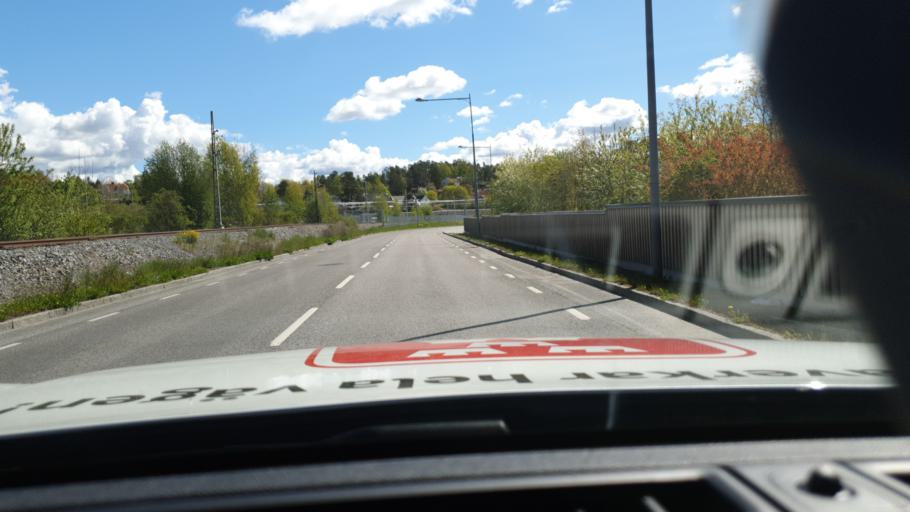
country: SE
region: Stockholm
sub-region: Stockholms Kommun
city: Kista
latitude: 59.3869
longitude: 17.8875
